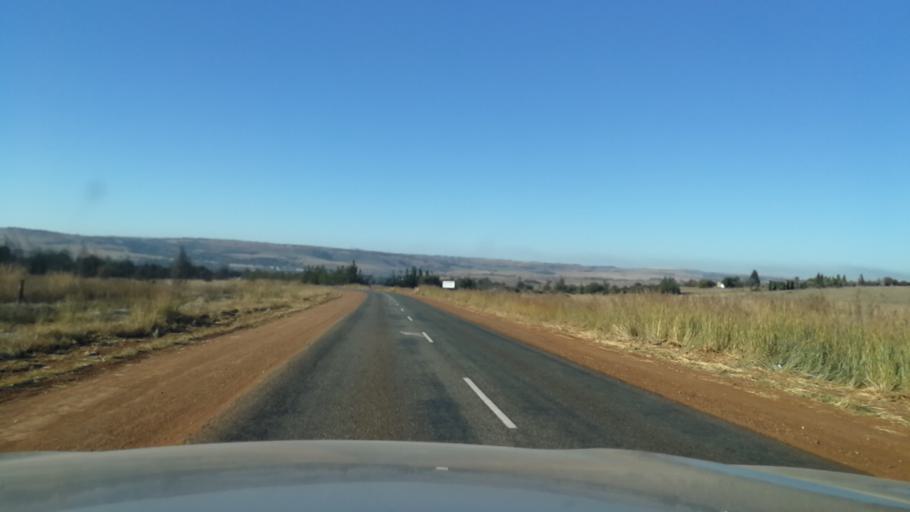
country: ZA
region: Gauteng
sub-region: West Rand District Municipality
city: Krugersdorp
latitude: -25.9992
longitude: 27.7014
